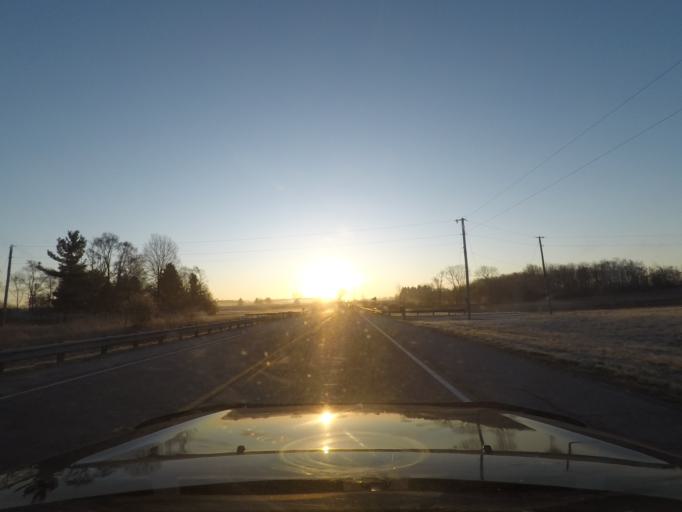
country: US
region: Indiana
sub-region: Saint Joseph County
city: North Liberty
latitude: 41.4487
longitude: -86.3557
